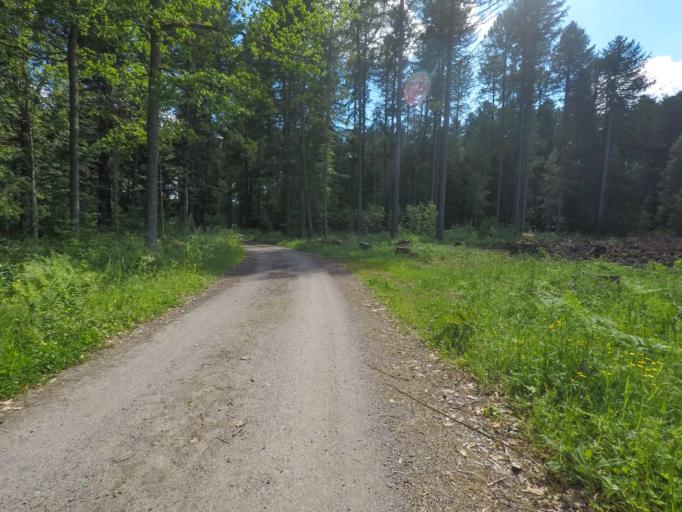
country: FI
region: Southern Savonia
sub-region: Savonlinna
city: Punkaharju
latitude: 61.8092
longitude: 29.3188
